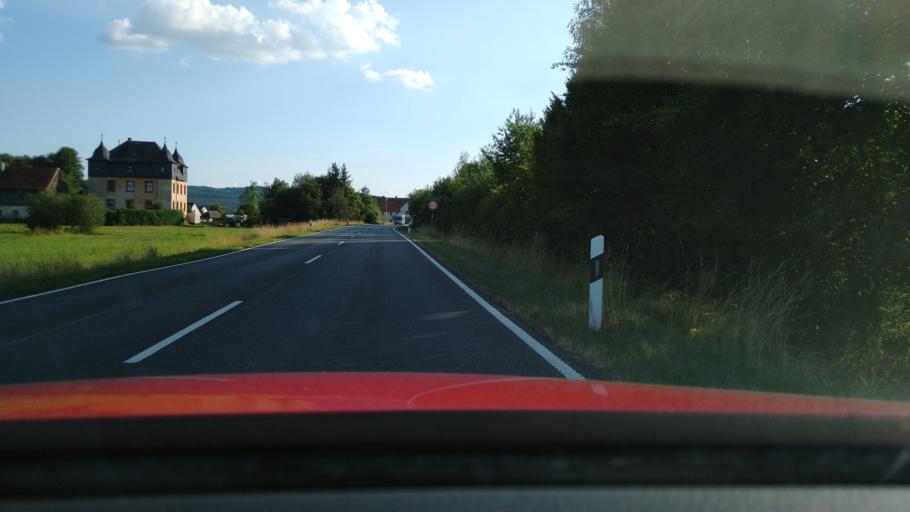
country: DE
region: Bavaria
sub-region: Upper Franconia
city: Plankenfels
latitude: 49.9096
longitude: 11.3741
